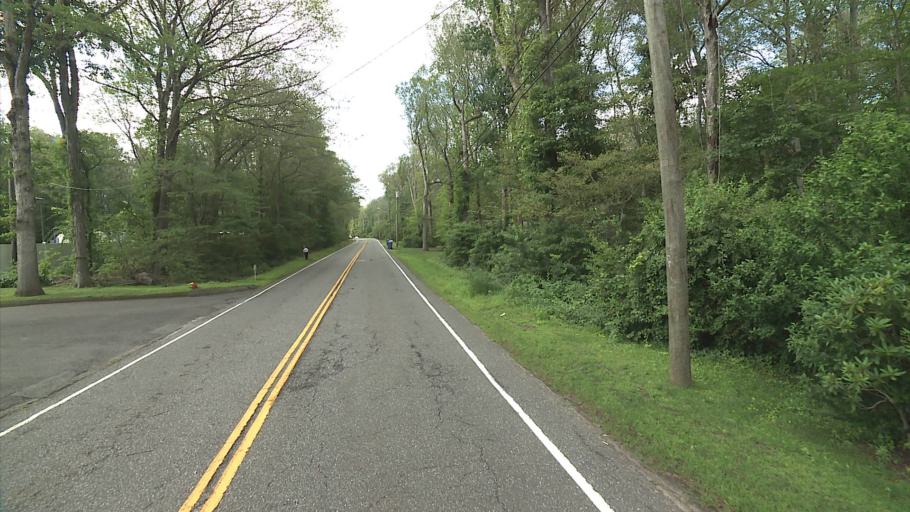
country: US
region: Connecticut
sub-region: Middlesex County
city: Chester Center
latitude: 41.3848
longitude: -72.5091
